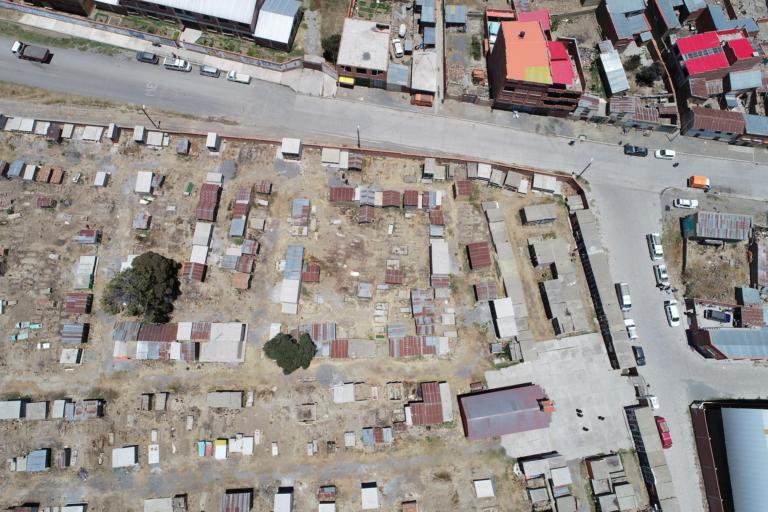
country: BO
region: La Paz
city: Achacachi
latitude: -16.0458
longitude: -68.6898
